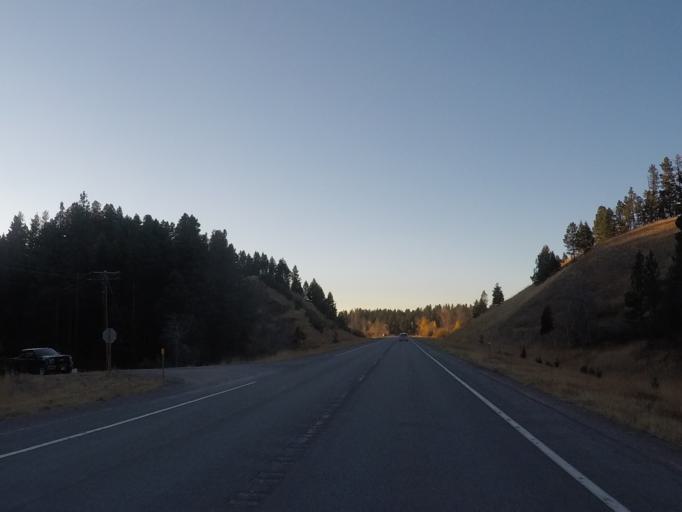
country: US
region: Montana
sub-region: Lewis and Clark County
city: Lincoln
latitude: 47.0133
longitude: -113.0667
